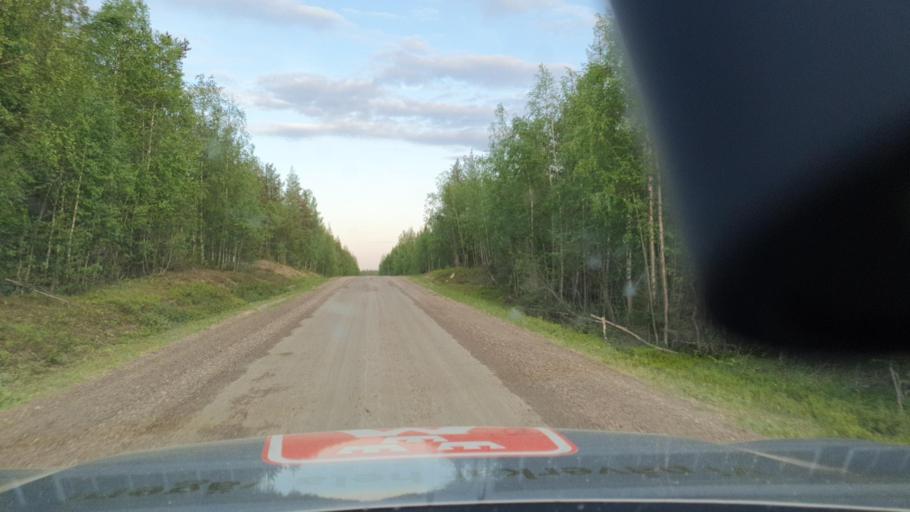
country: SE
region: Norrbotten
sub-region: Bodens Kommun
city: Boden
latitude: 66.5124
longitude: 21.5275
